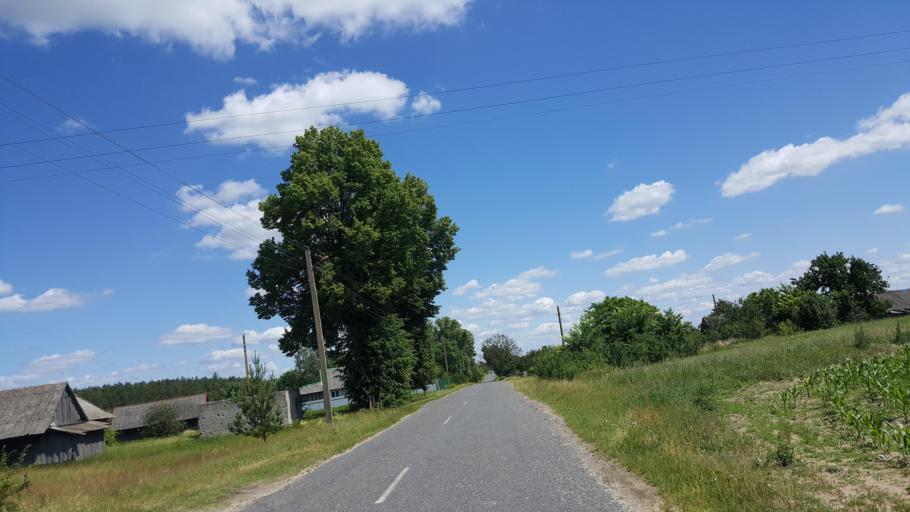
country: PL
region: Podlasie
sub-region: Powiat hajnowski
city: Czeremcha
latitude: 52.5135
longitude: 23.5398
